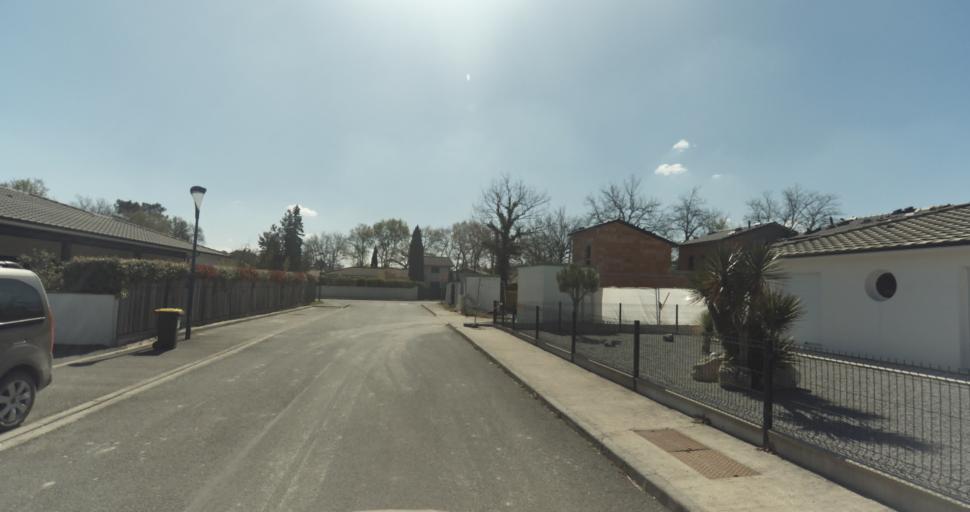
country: FR
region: Aquitaine
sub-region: Departement de la Gironde
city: Martignas-sur-Jalle
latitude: 44.8005
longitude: -0.7904
